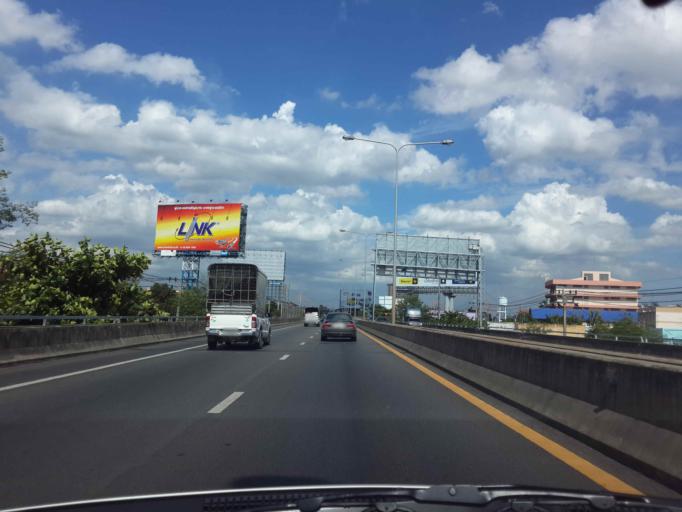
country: TH
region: Bangkok
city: Rat Burana
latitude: 13.6706
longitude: 100.5010
